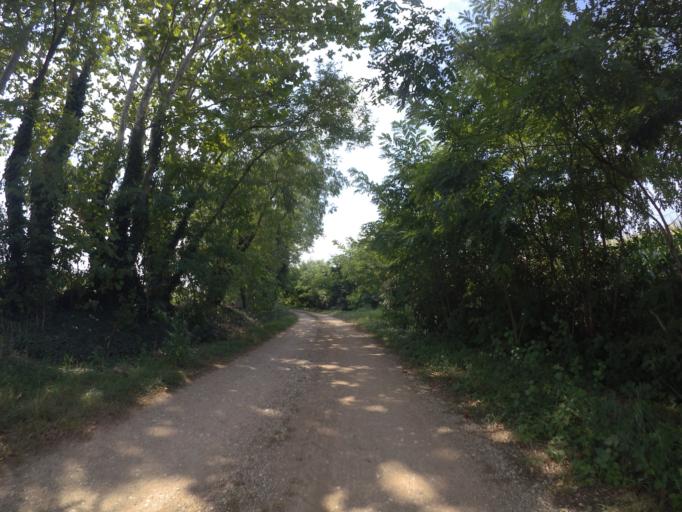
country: IT
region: Friuli Venezia Giulia
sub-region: Provincia di Udine
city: Bertiolo
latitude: 45.9568
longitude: 13.0735
